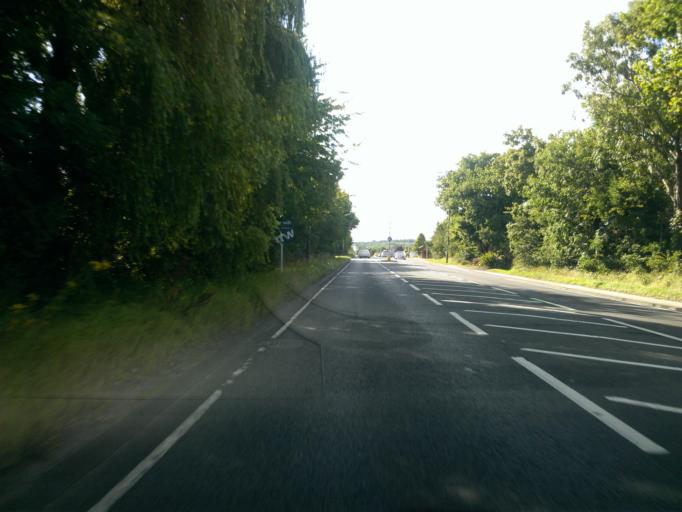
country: GB
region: England
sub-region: Warwickshire
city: Atherstone
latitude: 52.5889
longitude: -1.5850
